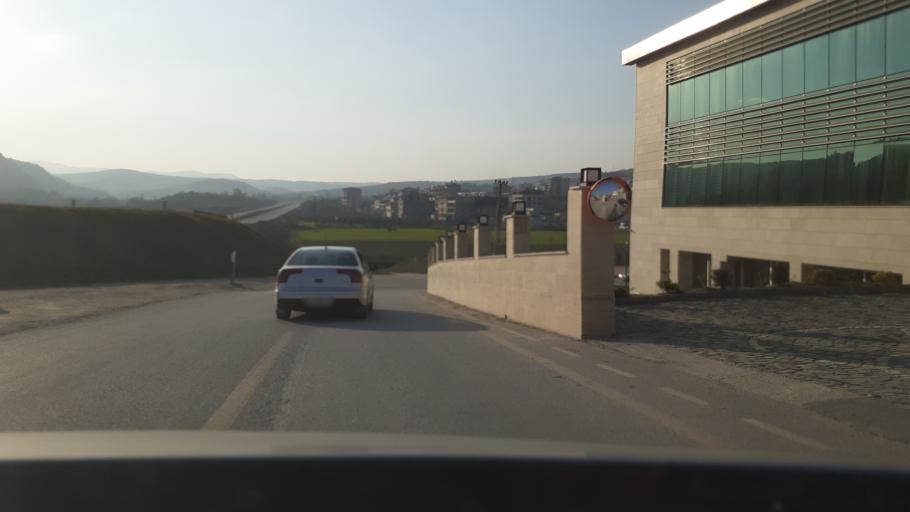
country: TR
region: Hatay
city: Fatikli
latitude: 36.1119
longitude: 36.2629
